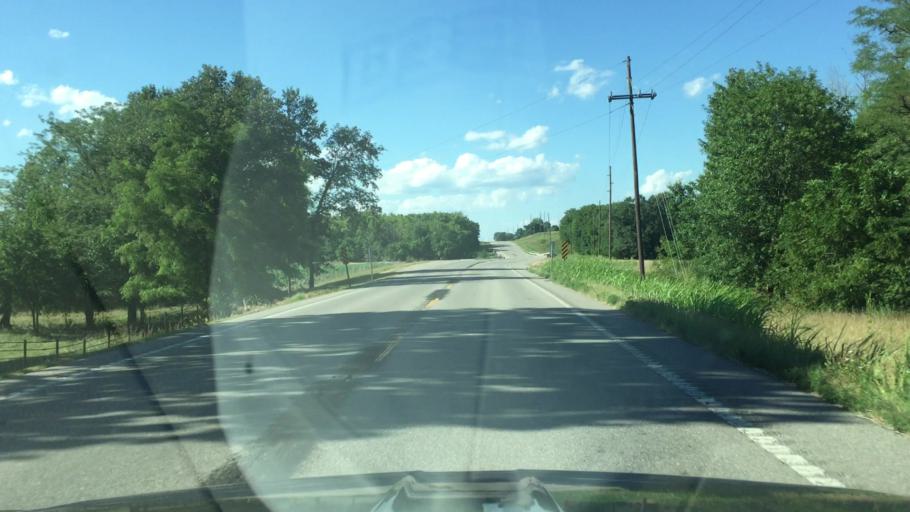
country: US
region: Missouri
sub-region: Moniteau County
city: Tipton
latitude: 38.6280
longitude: -92.7894
